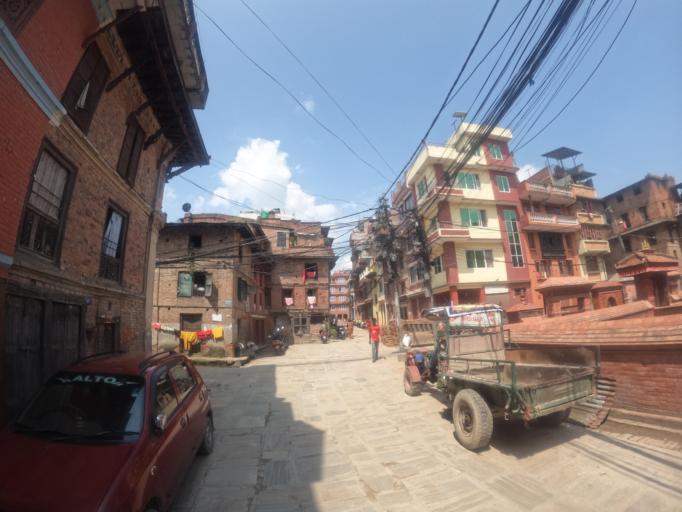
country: NP
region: Central Region
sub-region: Bagmati Zone
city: Bhaktapur
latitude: 27.6908
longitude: 85.3888
